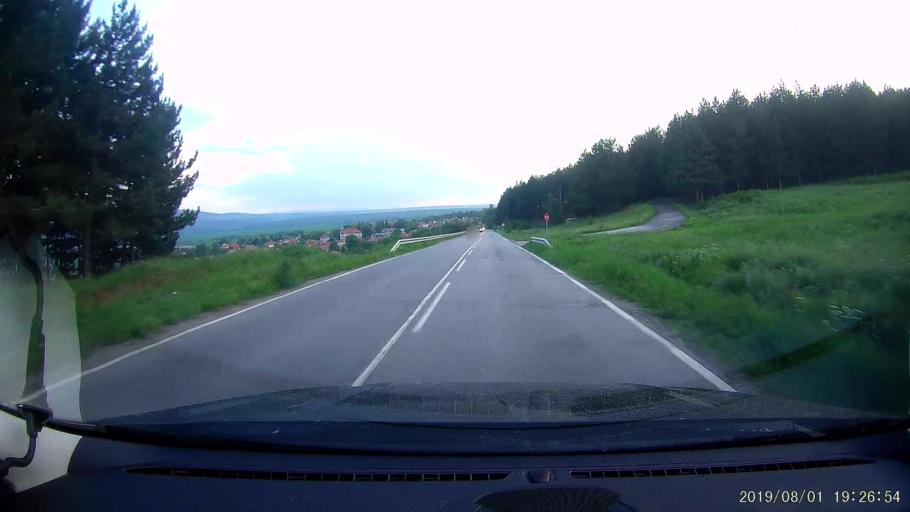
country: BG
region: Burgas
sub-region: Obshtina Sungurlare
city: Sungurlare
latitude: 42.8535
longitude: 26.9360
